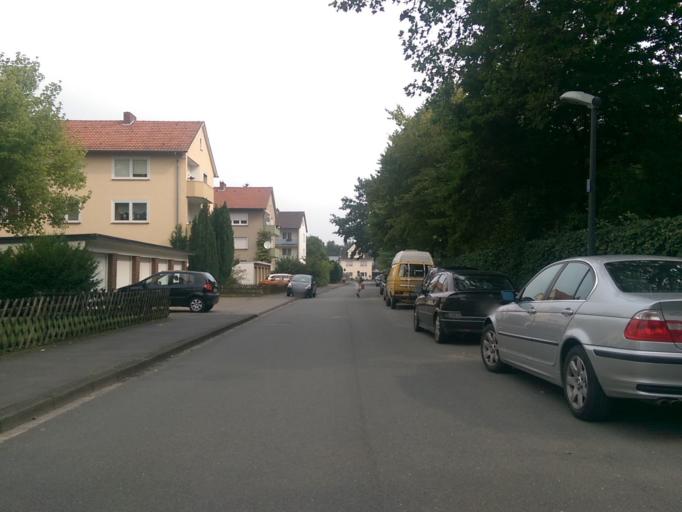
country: DE
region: North Rhine-Westphalia
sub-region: Regierungsbezirk Detmold
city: Guetersloh
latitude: 51.8986
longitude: 8.3639
